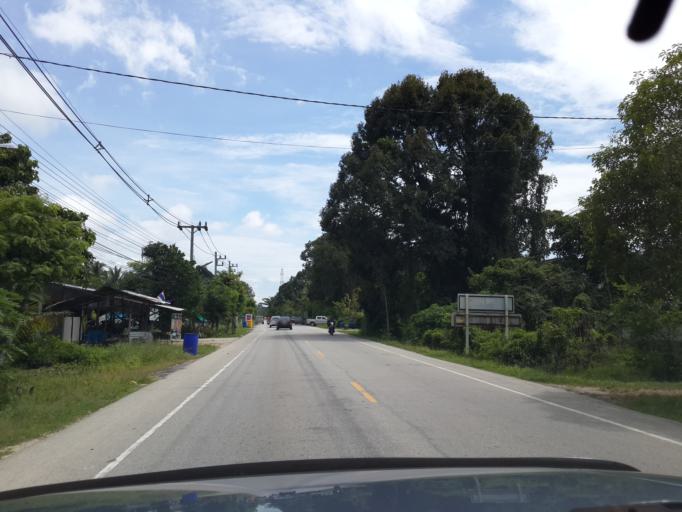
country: TH
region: Narathiwat
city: Narathiwat
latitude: 6.4421
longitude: 101.7975
